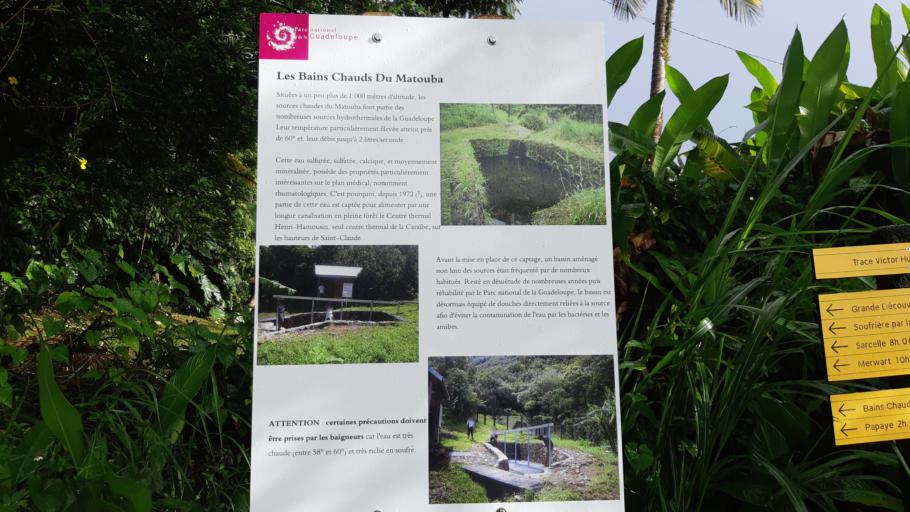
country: GP
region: Guadeloupe
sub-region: Guadeloupe
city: Saint-Claude
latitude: 16.0467
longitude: -61.6918
